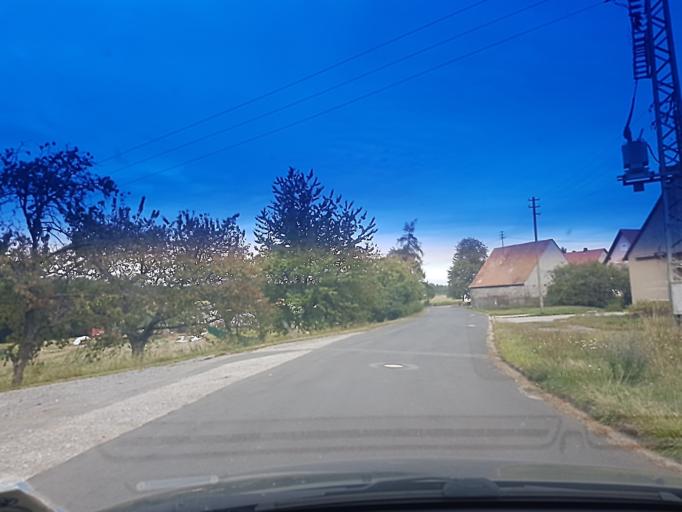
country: DE
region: Bavaria
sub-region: Upper Franconia
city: Burgwindheim
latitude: 49.8693
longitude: 10.5265
